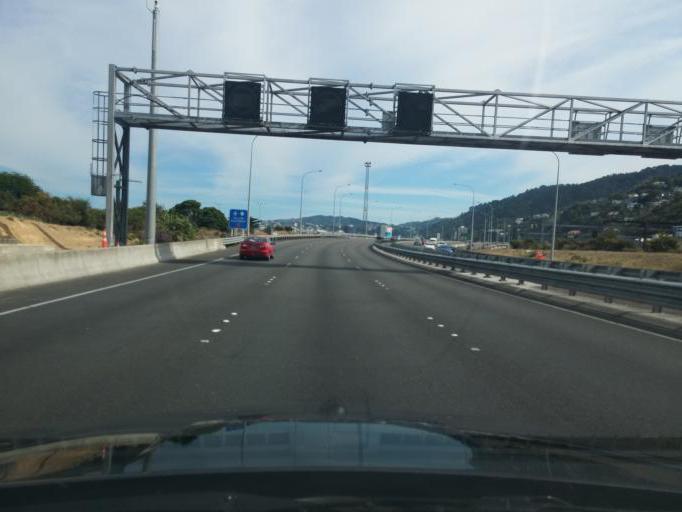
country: NZ
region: Wellington
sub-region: Wellington City
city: Wellington
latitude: -41.2604
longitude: 174.7918
